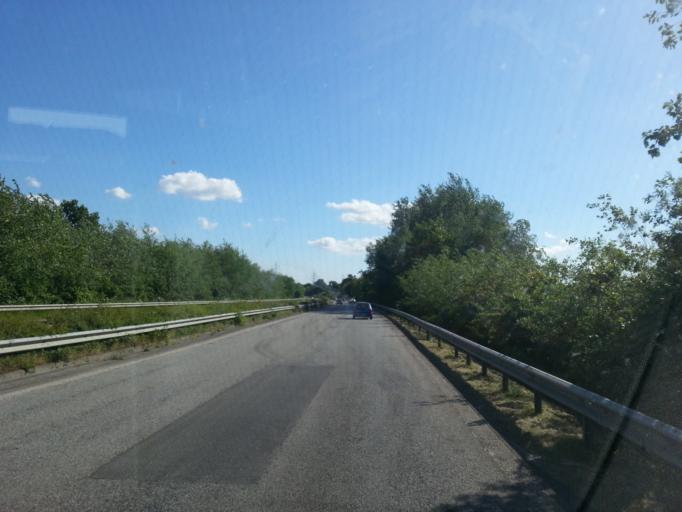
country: DE
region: Schleswig-Holstein
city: Neustadt in Holstein
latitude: 54.1158
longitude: 10.7860
